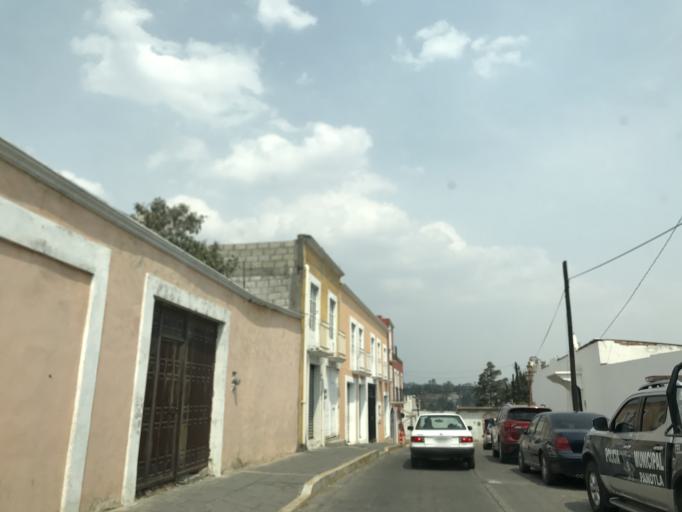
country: MX
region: Tlaxcala
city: Panotla
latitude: 19.3149
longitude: -98.2670
